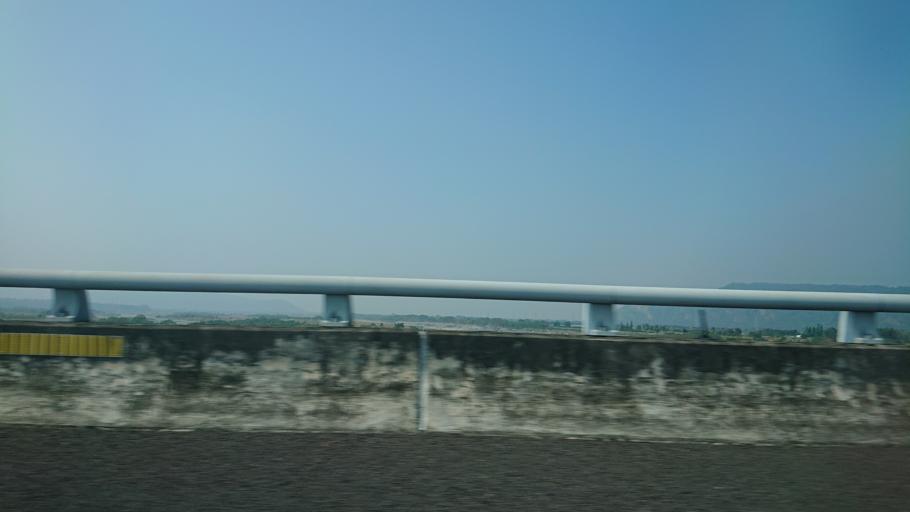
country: TW
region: Taiwan
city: Lugu
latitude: 23.8043
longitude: 120.6978
